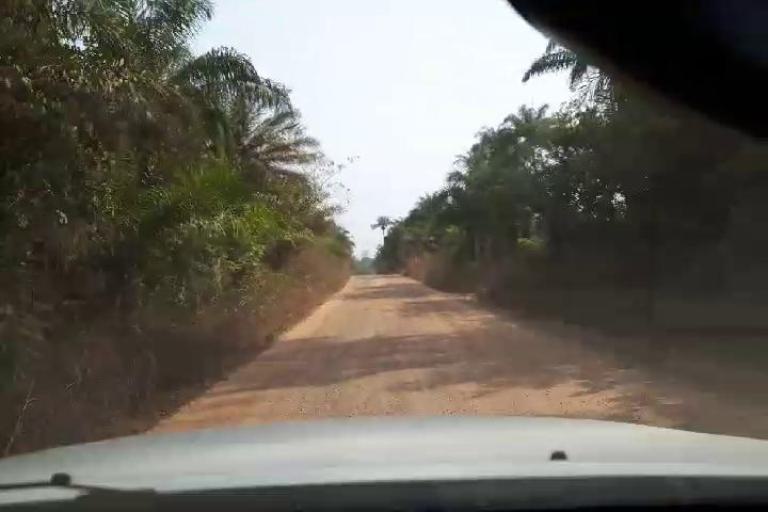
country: SL
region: Northern Province
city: Masingbi
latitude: 8.7722
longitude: -11.8763
